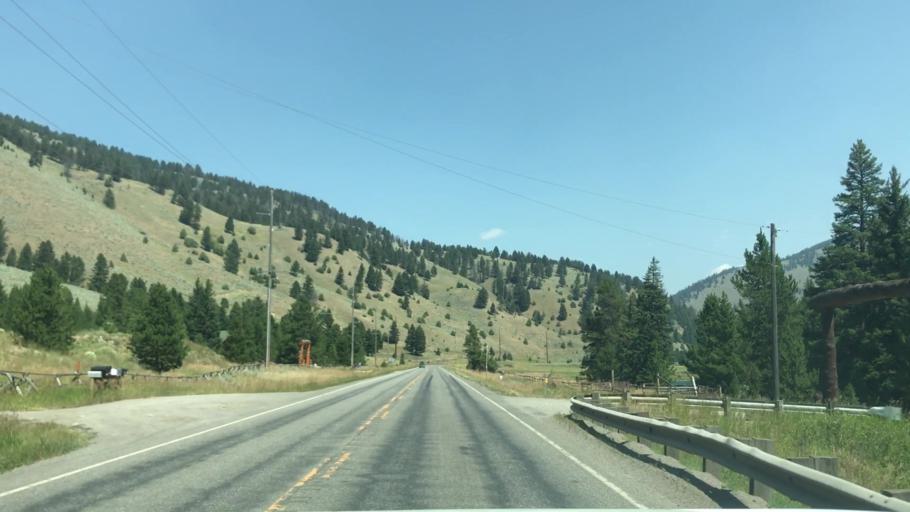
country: US
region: Montana
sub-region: Gallatin County
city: Big Sky
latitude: 45.2726
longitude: -111.2416
